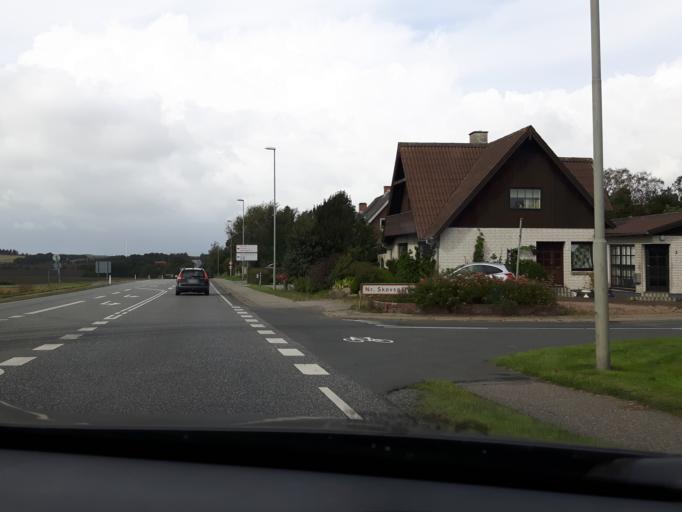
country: DK
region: North Denmark
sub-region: Jammerbugt Kommune
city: Brovst
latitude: 57.0954
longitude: 9.4896
